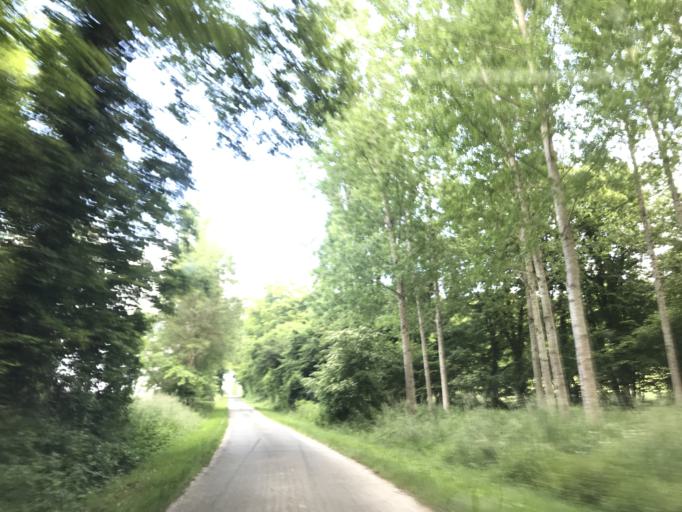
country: FR
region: Aquitaine
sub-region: Departement de la Dordogne
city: Saint-Aulaye
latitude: 45.2639
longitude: 0.1245
